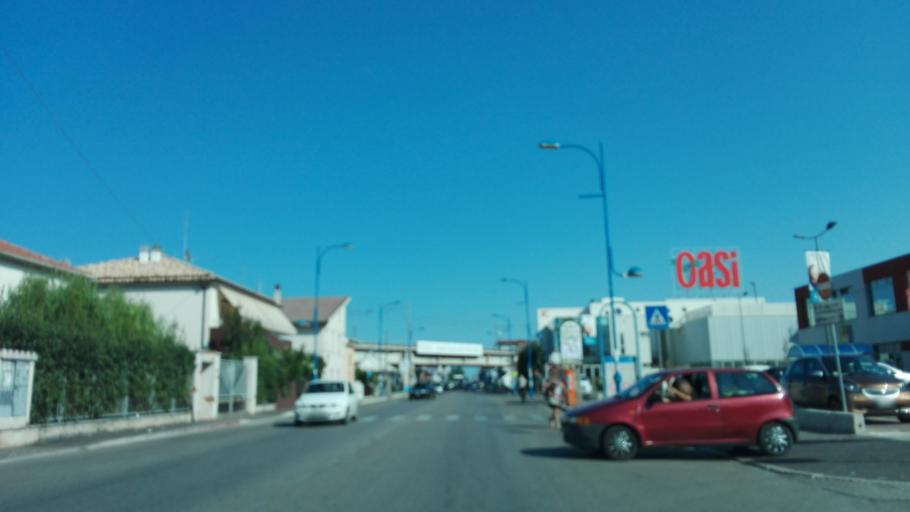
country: IT
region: Abruzzo
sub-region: Provincia di Pescara
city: Montesilvano Marina
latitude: 42.5090
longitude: 14.1590
